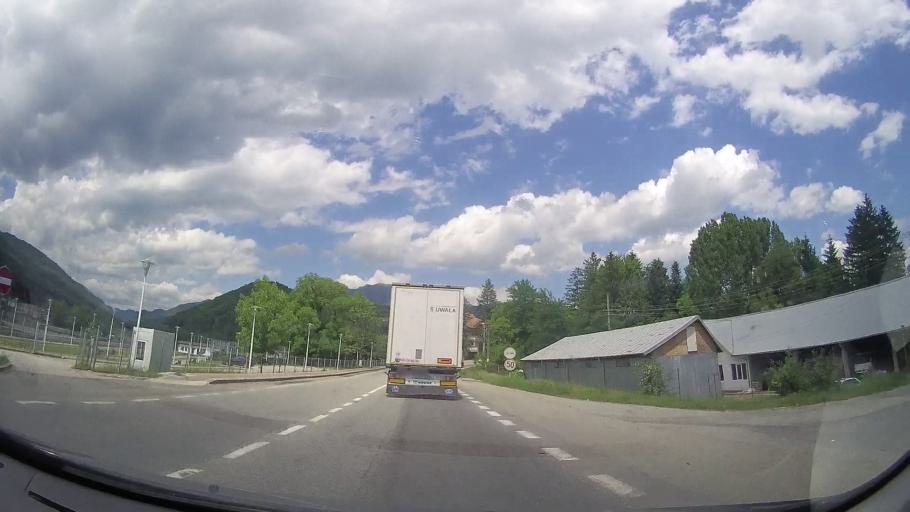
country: RO
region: Valcea
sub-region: Oras Calimanesti
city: Jiblea Veche
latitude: 45.2415
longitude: 24.3479
